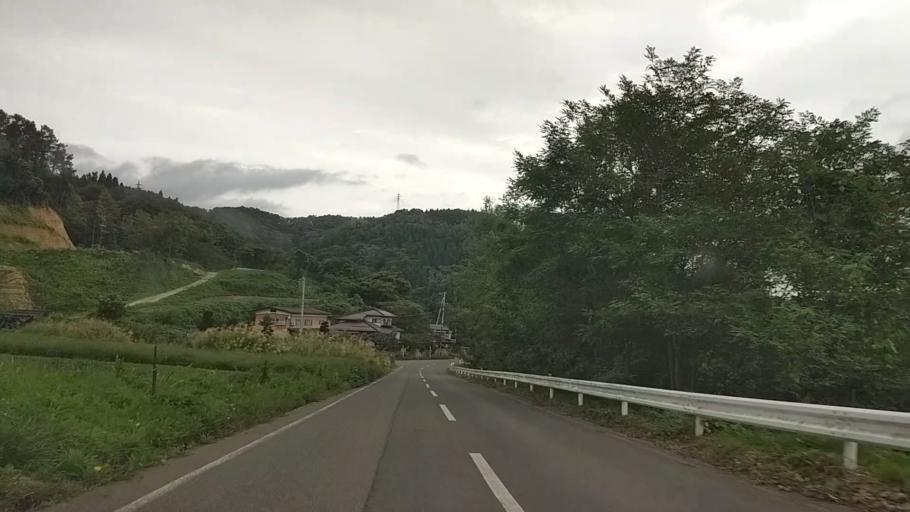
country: JP
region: Nagano
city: Nakano
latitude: 36.7848
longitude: 138.3331
